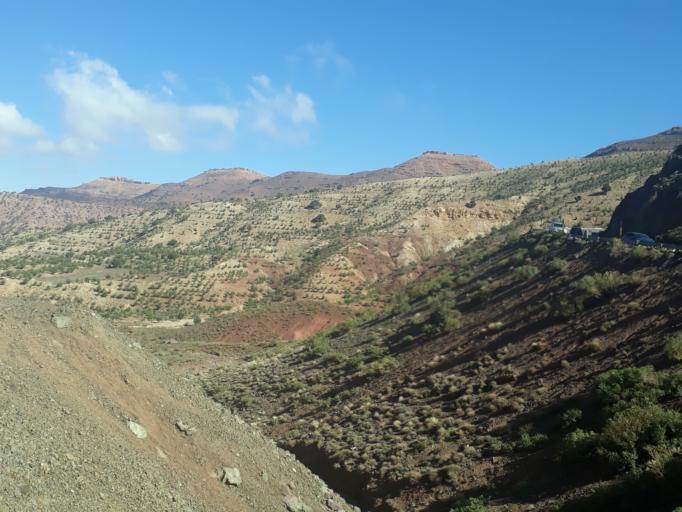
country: MA
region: Souss-Massa-Draa
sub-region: Ouarzazate
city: Telouet
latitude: 31.2621
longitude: -7.3960
